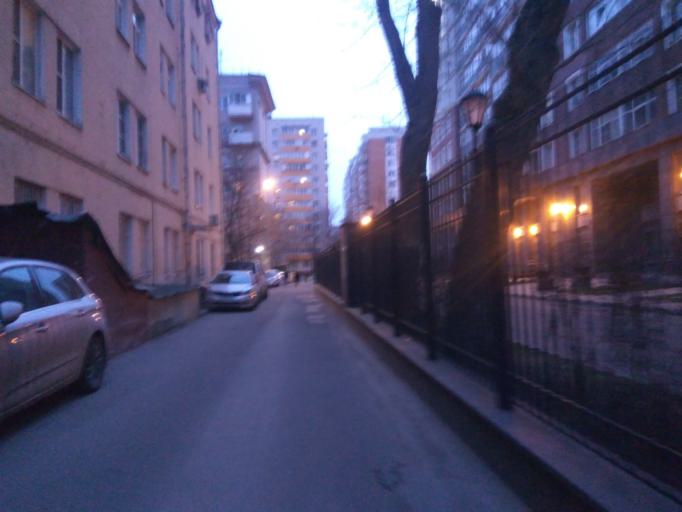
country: RU
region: Moscow
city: Zamoskvorech'ye
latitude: 55.7212
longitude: 37.6189
